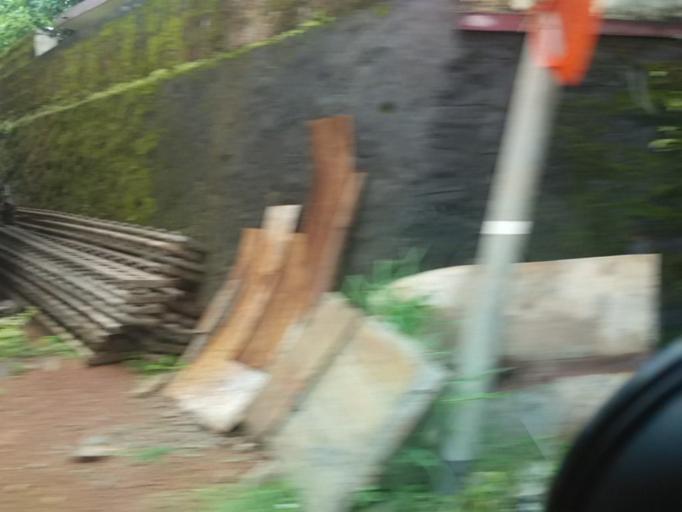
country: IN
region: Kerala
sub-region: Kozhikode
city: Kozhikode
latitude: 11.2762
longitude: 75.8117
